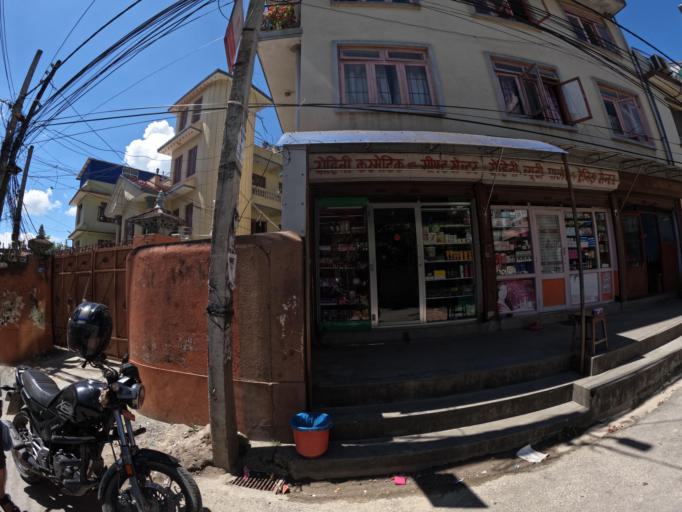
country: NP
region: Central Region
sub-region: Bagmati Zone
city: Kathmandu
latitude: 27.7387
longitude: 85.3236
